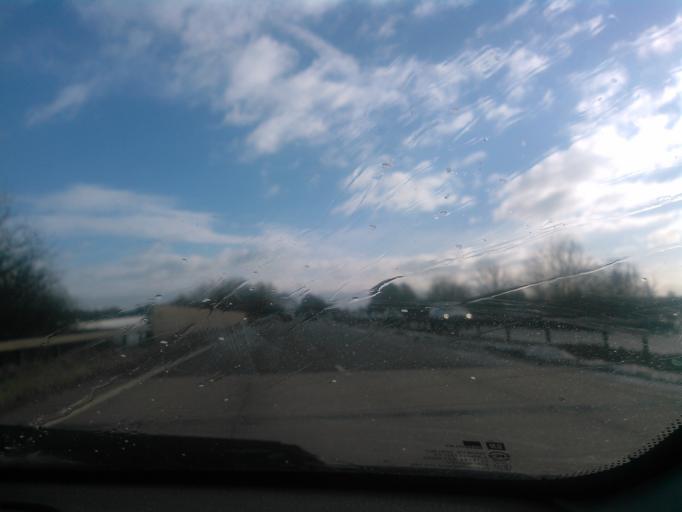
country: GB
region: England
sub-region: Staffordshire
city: Cheadle
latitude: 52.9514
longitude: -2.0189
